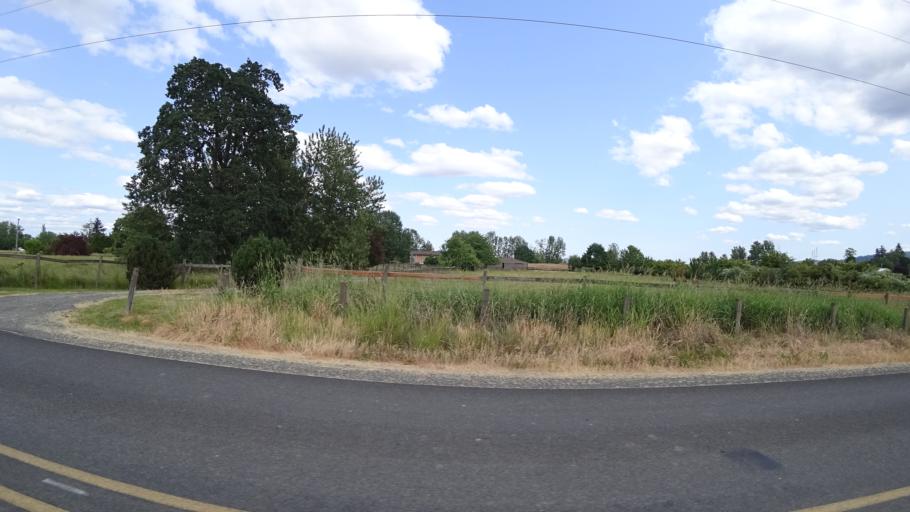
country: US
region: Oregon
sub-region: Washington County
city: Oak Hills
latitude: 45.6343
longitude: -122.7965
